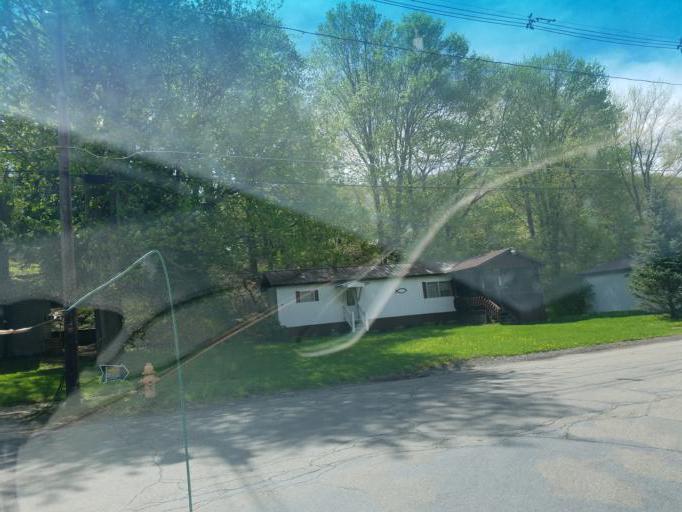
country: US
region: Pennsylvania
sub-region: Potter County
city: Galeton
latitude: 41.7365
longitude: -77.6341
